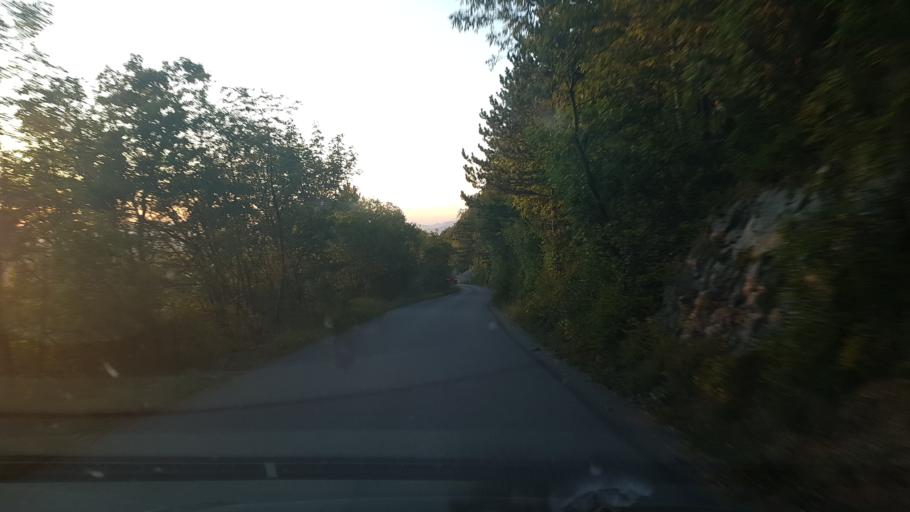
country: SI
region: Vipava
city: Vipava
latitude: 45.7939
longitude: 14.0083
